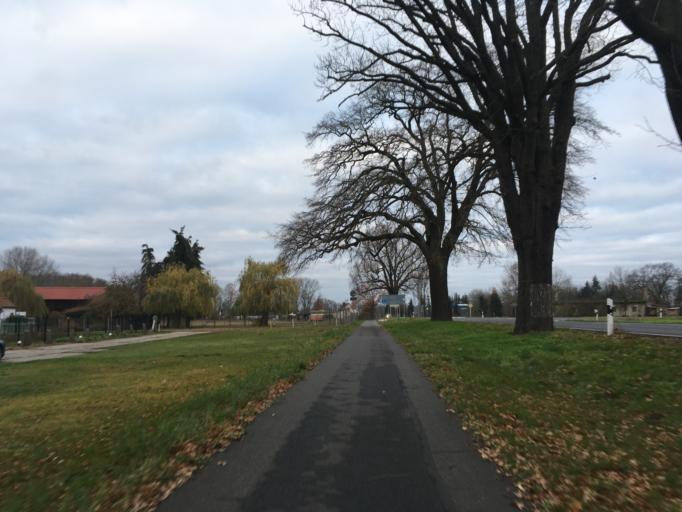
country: DE
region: Brandenburg
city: Seelow
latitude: 52.5801
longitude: 14.3390
